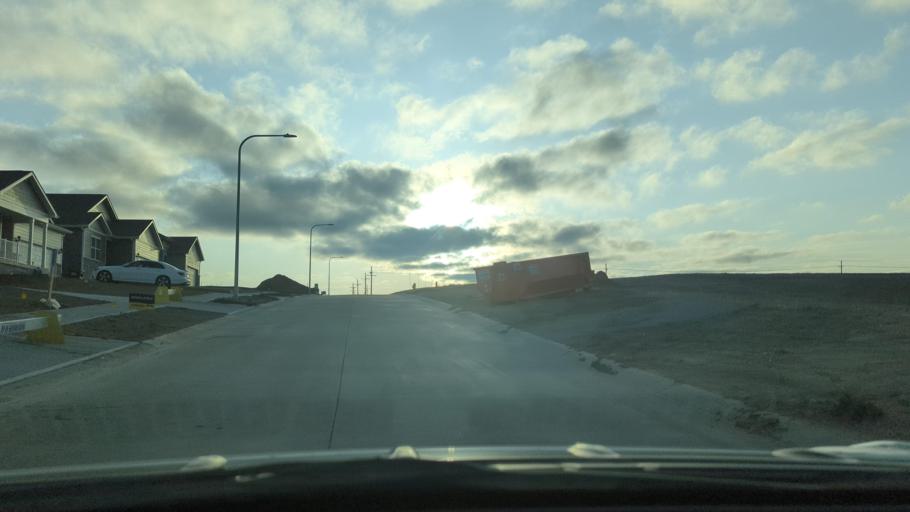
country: US
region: Nebraska
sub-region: Sarpy County
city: Offutt Air Force Base
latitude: 41.1181
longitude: -95.9788
